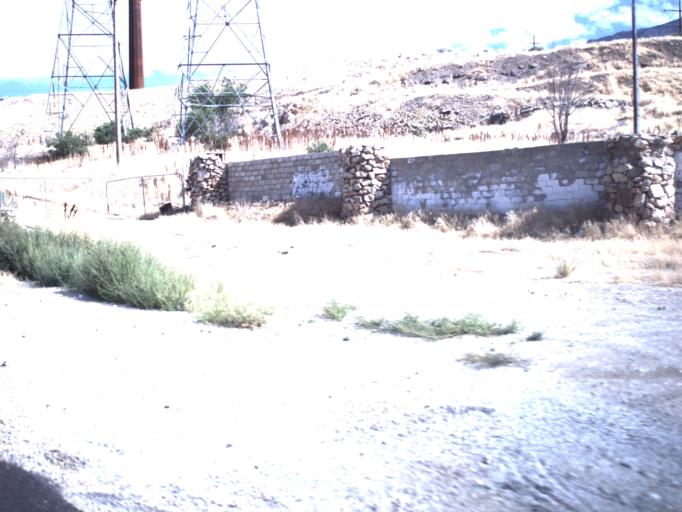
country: US
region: Utah
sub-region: Box Elder County
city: South Willard
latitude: 41.3362
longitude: -112.0279
